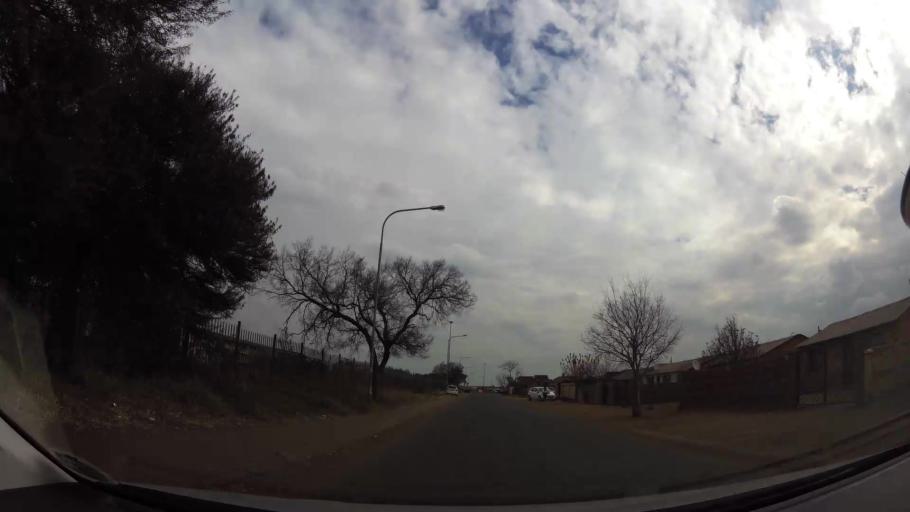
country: ZA
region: Gauteng
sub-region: City of Johannesburg Metropolitan Municipality
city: Soweto
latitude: -26.2635
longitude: 27.8563
